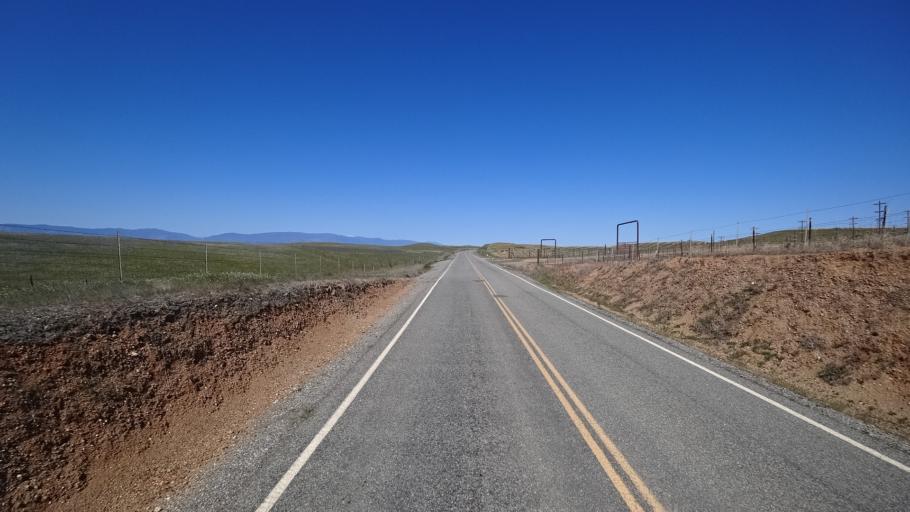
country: US
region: California
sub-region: Glenn County
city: Orland
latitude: 39.8277
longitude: -122.3372
